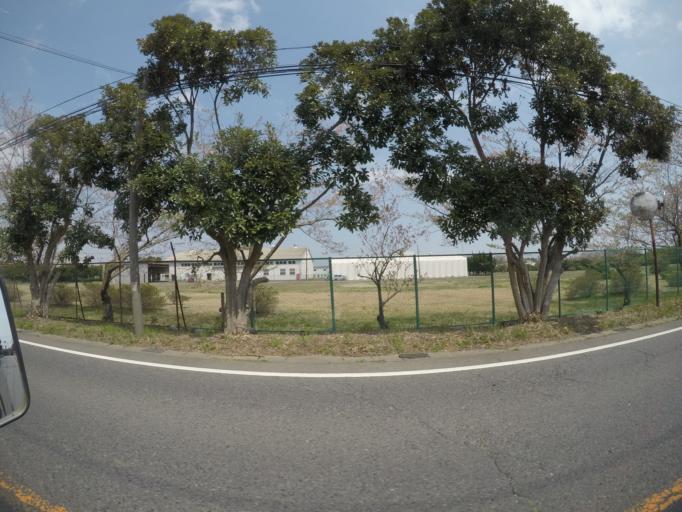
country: JP
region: Chiba
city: Sawara
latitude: 35.8584
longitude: 140.5553
